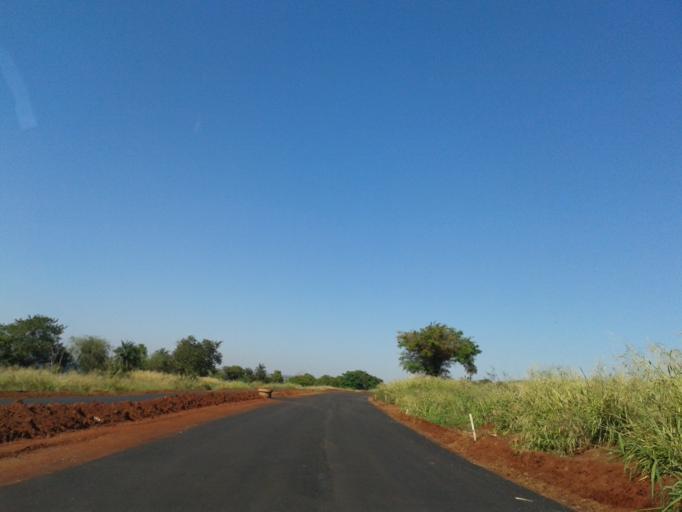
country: BR
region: Minas Gerais
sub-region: Capinopolis
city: Capinopolis
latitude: -18.5324
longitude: -49.4973
